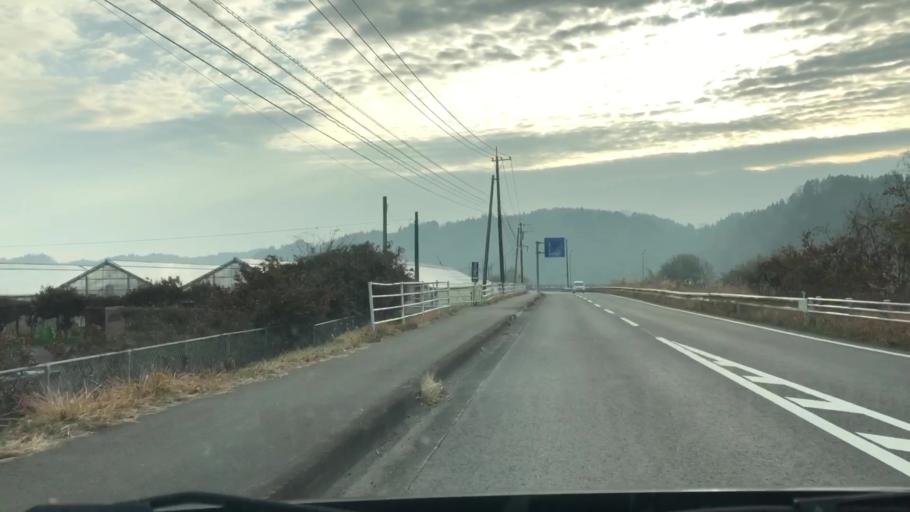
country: JP
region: Oita
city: Takedamachi
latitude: 32.9657
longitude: 131.4821
